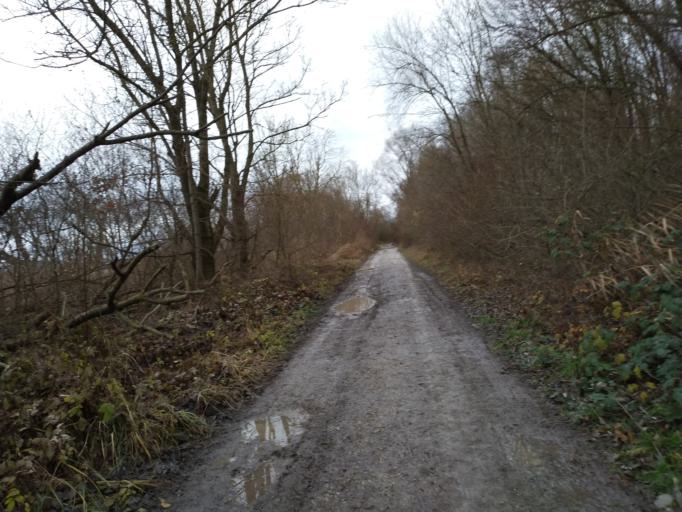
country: DE
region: Bavaria
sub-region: Swabia
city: Bachingen an der Brenz
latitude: 48.4996
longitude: 10.3013
